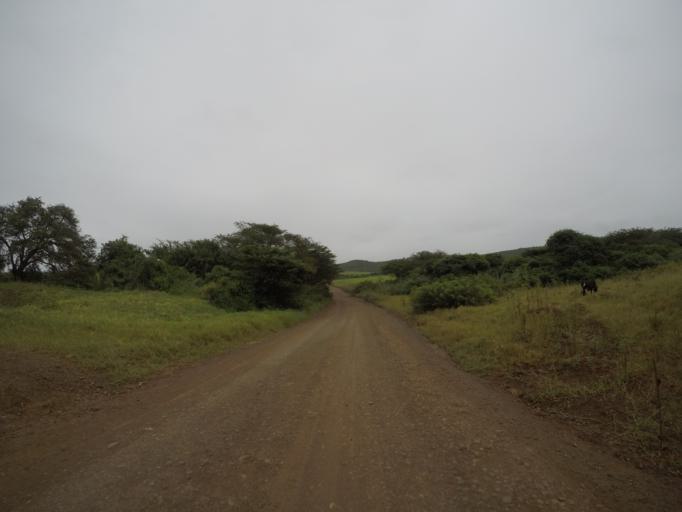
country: ZA
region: KwaZulu-Natal
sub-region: uThungulu District Municipality
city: Empangeni
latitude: -28.6585
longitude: 31.7918
